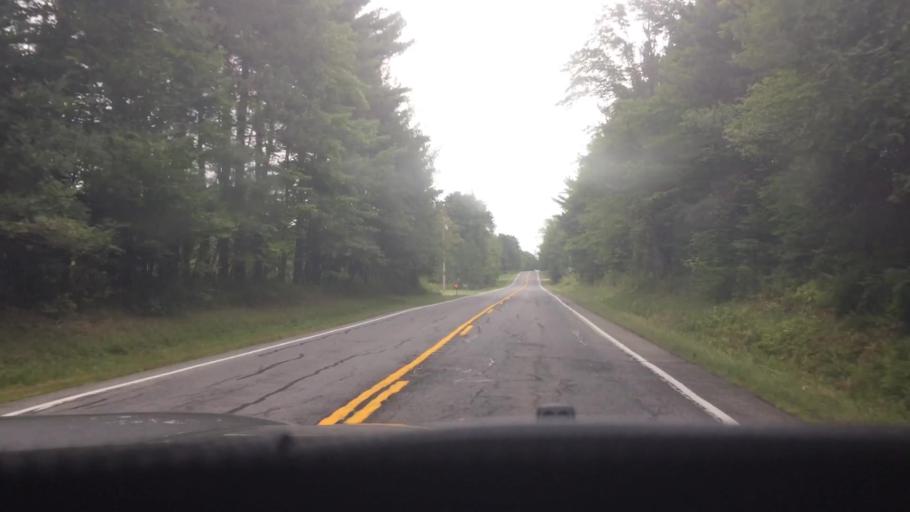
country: US
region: New York
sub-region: St. Lawrence County
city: Hannawa Falls
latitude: 44.6665
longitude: -74.7400
